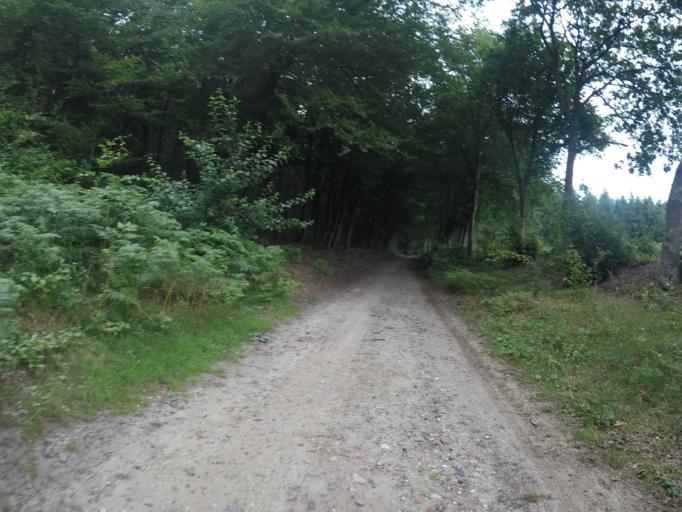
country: DE
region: Lower Saxony
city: Wingst
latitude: 53.7211
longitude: 9.0691
